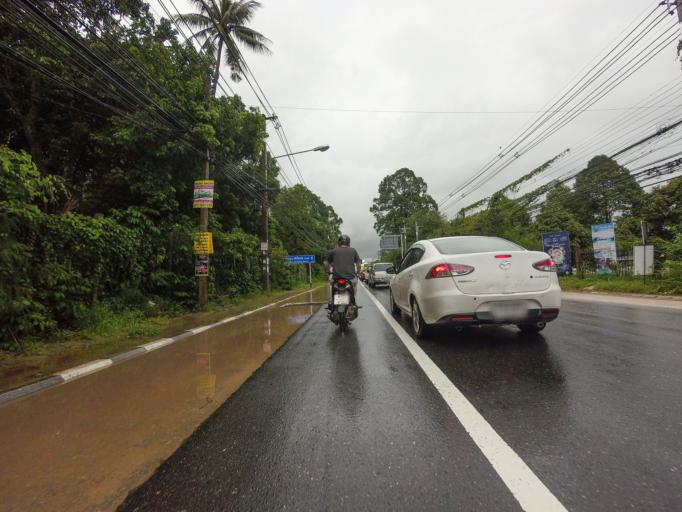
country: TH
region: Surat Thani
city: Ko Samui
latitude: 9.5150
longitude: 100.0503
